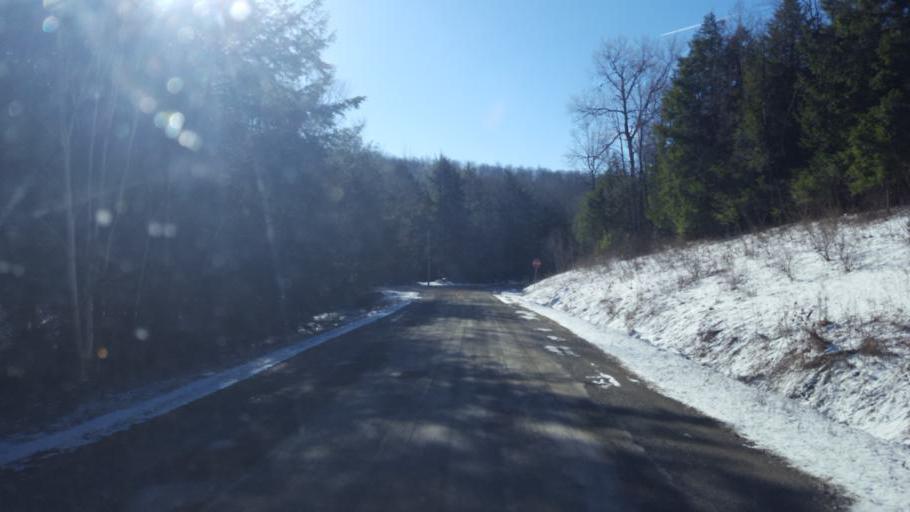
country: US
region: New York
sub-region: Allegany County
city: Wellsville
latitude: 42.1478
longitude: -77.9072
